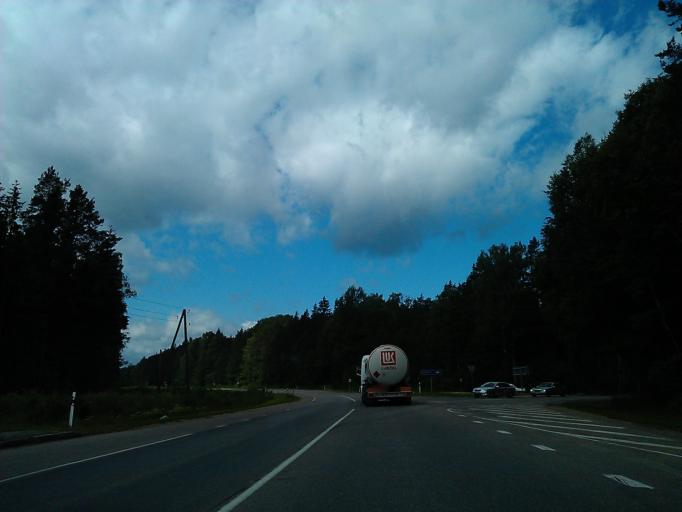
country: LV
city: Tireli
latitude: 56.9332
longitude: 23.4882
